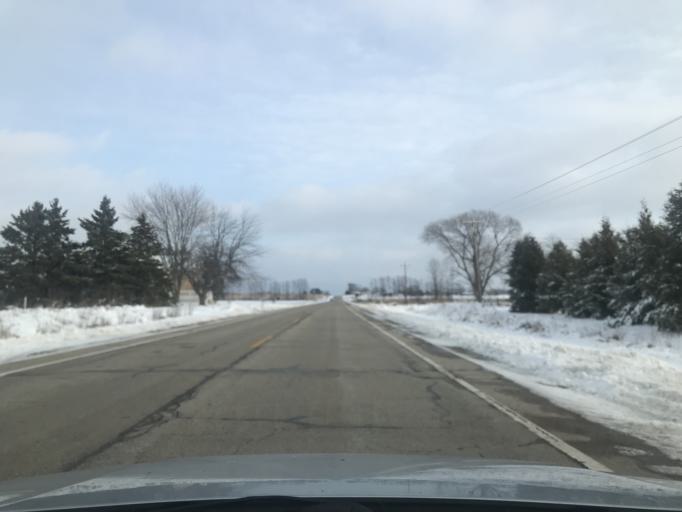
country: US
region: Wisconsin
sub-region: Oconto County
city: Oconto
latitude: 44.8931
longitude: -87.9796
